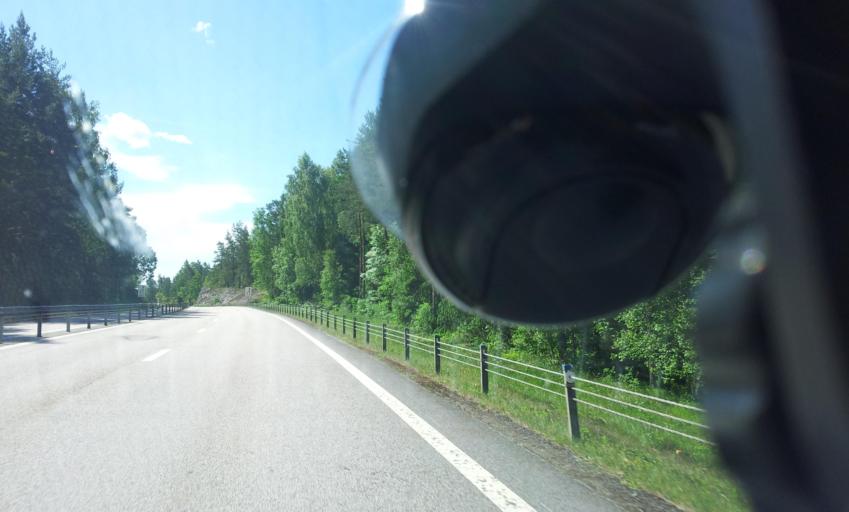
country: SE
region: Kalmar
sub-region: Vasterviks Kommun
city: Forserum
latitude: 58.0303
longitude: 16.5150
